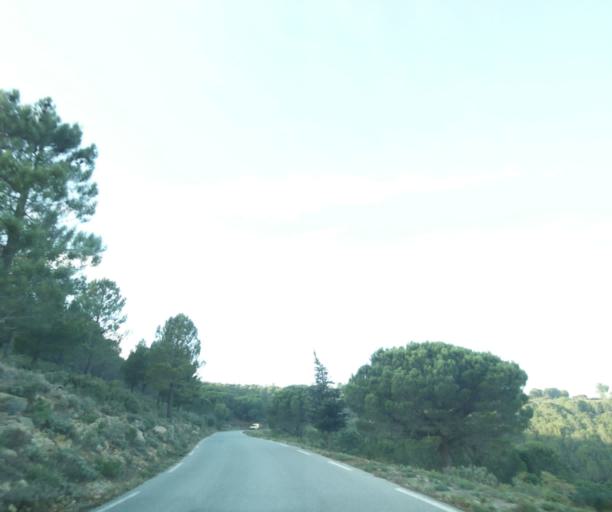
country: FR
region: Provence-Alpes-Cote d'Azur
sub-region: Departement des Bouches-du-Rhone
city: Cassis
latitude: 43.1944
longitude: 5.5565
